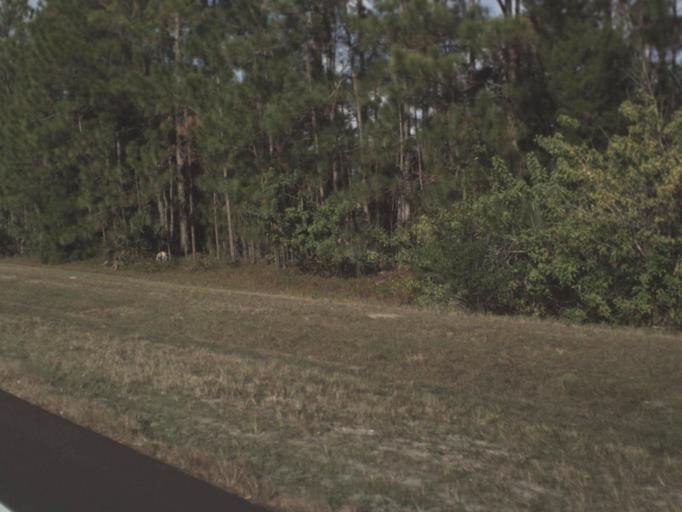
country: US
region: Florida
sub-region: Volusia County
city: South Daytona
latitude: 29.1498
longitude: -81.0621
